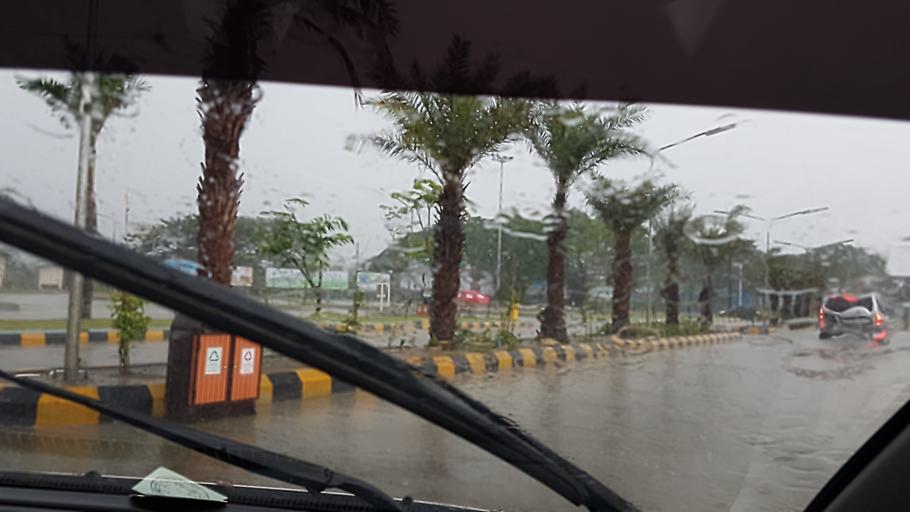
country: MM
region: Yangon
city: Syriam
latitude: 16.7735
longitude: 96.2003
